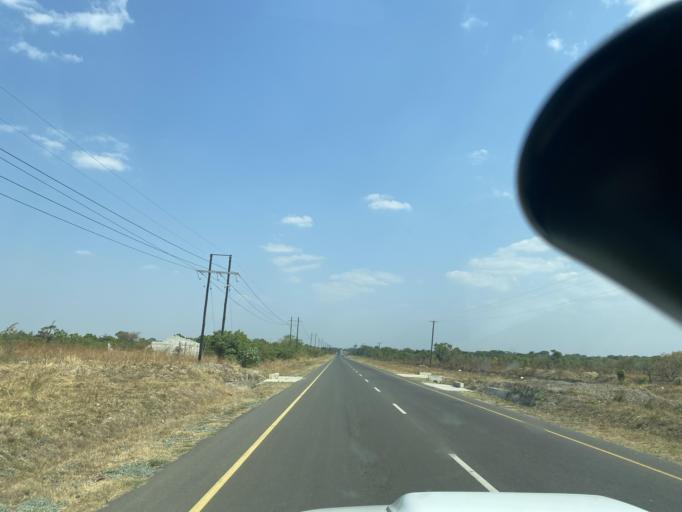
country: ZM
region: Lusaka
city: Lusaka
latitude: -15.3242
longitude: 28.0656
